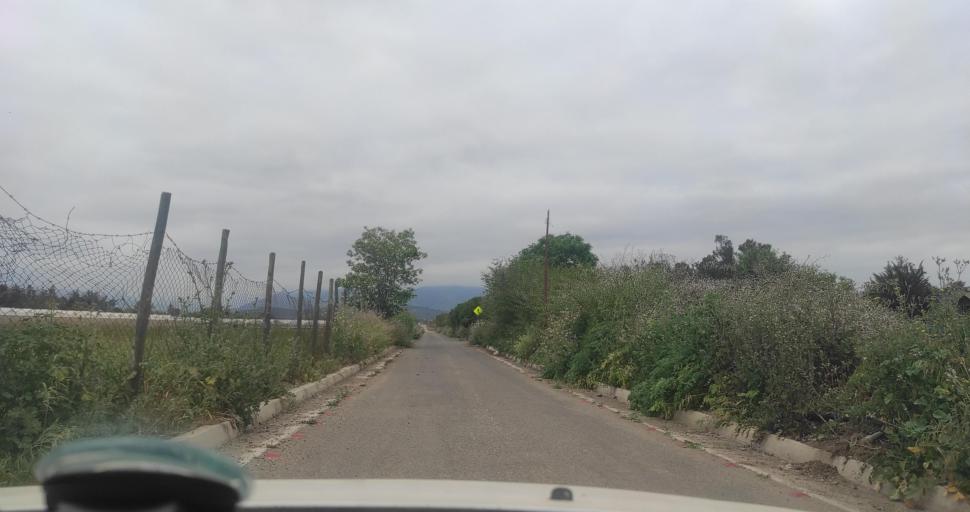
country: CL
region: Valparaiso
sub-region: Provincia de Marga Marga
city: Limache
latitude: -33.0174
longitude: -71.2396
